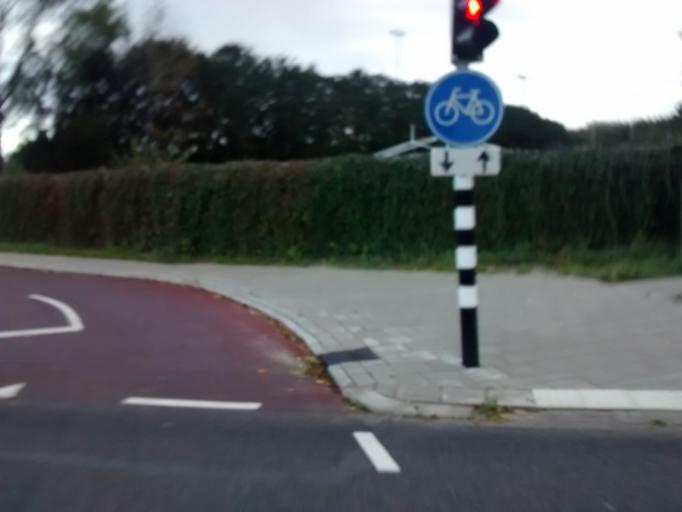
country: NL
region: Utrecht
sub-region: Gemeente Utrecht
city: Lunetten
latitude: 52.0725
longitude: 5.1481
